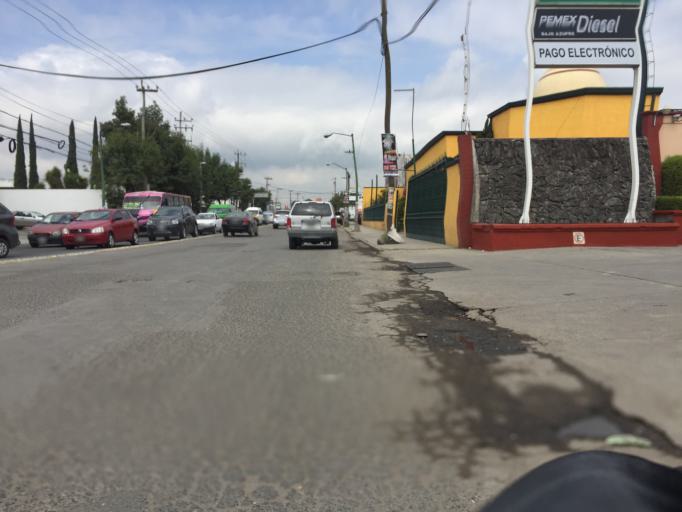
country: MX
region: Mexico
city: Cuautitlan
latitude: 19.6687
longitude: -99.1967
